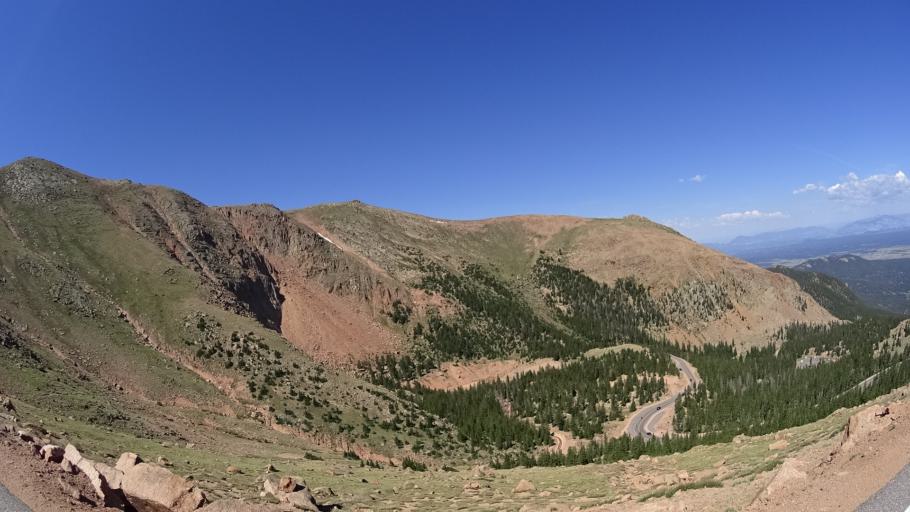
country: US
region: Colorado
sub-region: El Paso County
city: Cascade-Chipita Park
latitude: 38.8721
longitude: -105.0671
